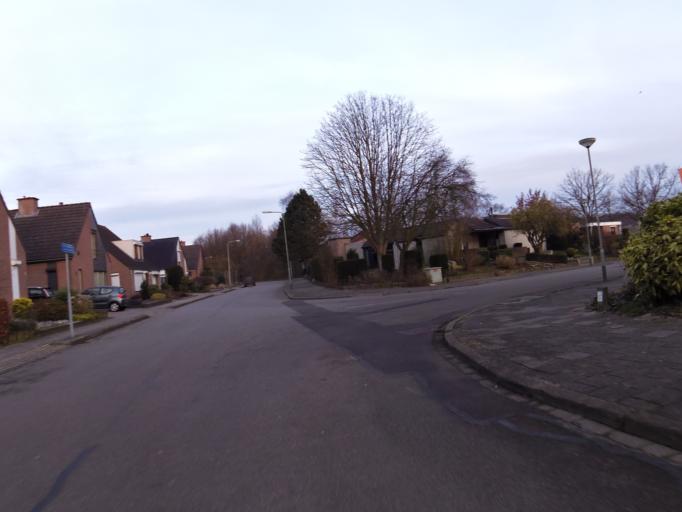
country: NL
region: Limburg
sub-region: Gemeente Kerkrade
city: Kerkrade
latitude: 50.8985
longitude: 6.0494
